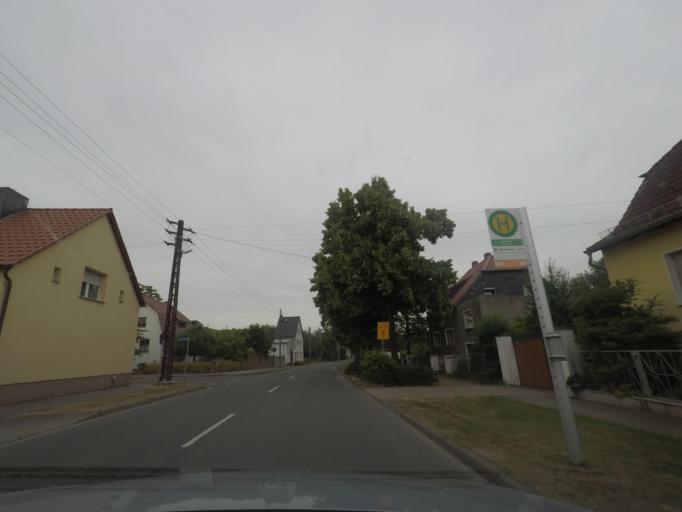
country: DE
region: Saxony-Anhalt
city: Seehausen
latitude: 52.1025
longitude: 11.2874
